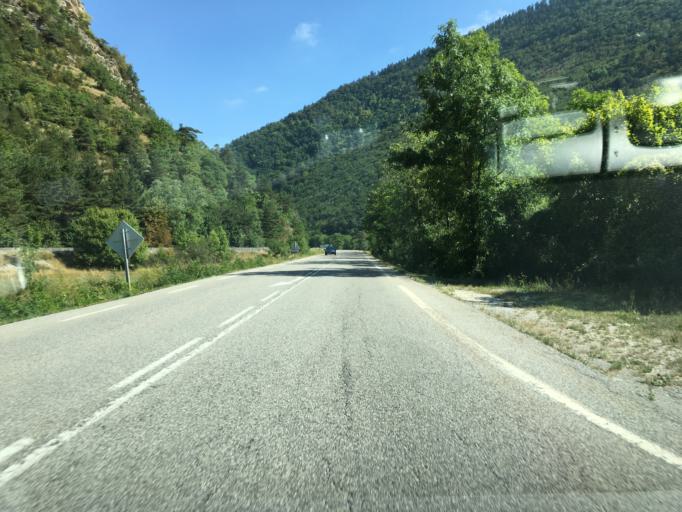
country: FR
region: Provence-Alpes-Cote d'Azur
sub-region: Departement des Hautes-Alpes
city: Veynes
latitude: 44.6429
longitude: 5.6998
